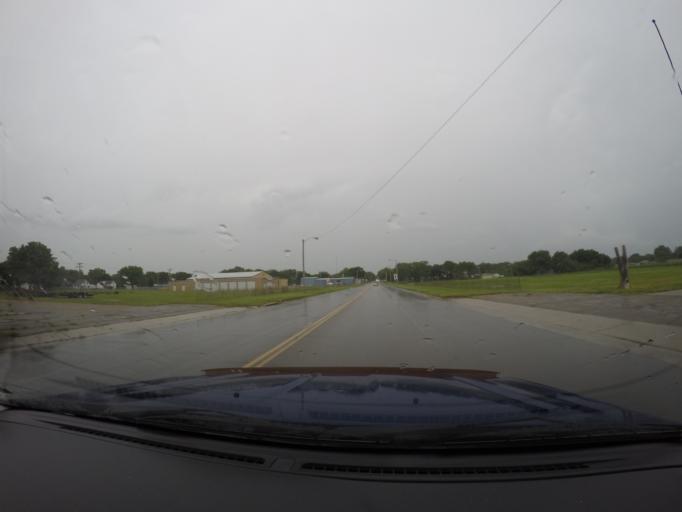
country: US
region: Kansas
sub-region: Cloud County
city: Concordia
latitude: 39.5716
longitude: -97.6426
